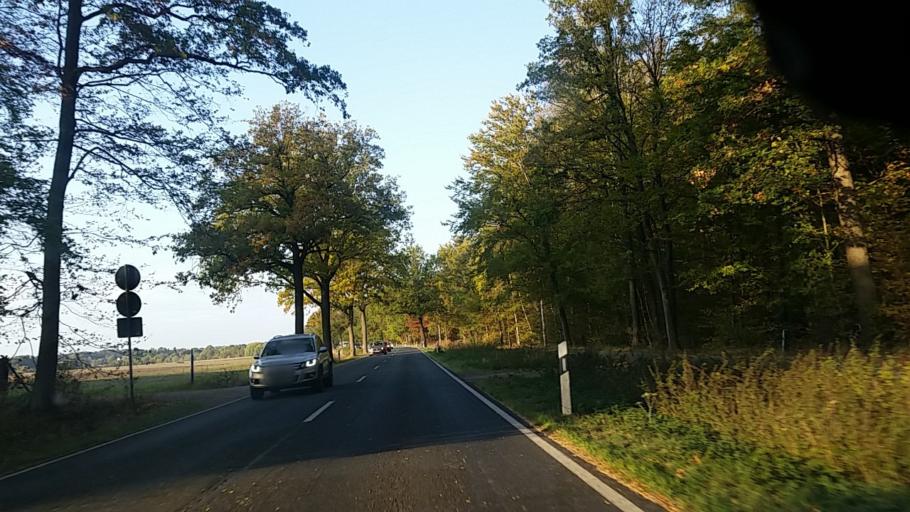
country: DE
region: Lower Saxony
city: Wolfsburg
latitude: 52.3791
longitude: 10.7424
